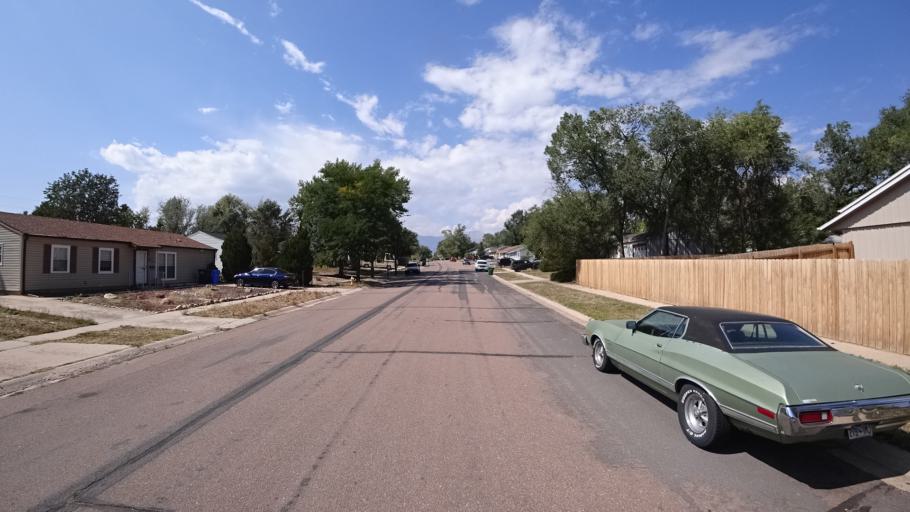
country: US
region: Colorado
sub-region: El Paso County
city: Colorado Springs
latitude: 38.8311
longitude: -104.7714
